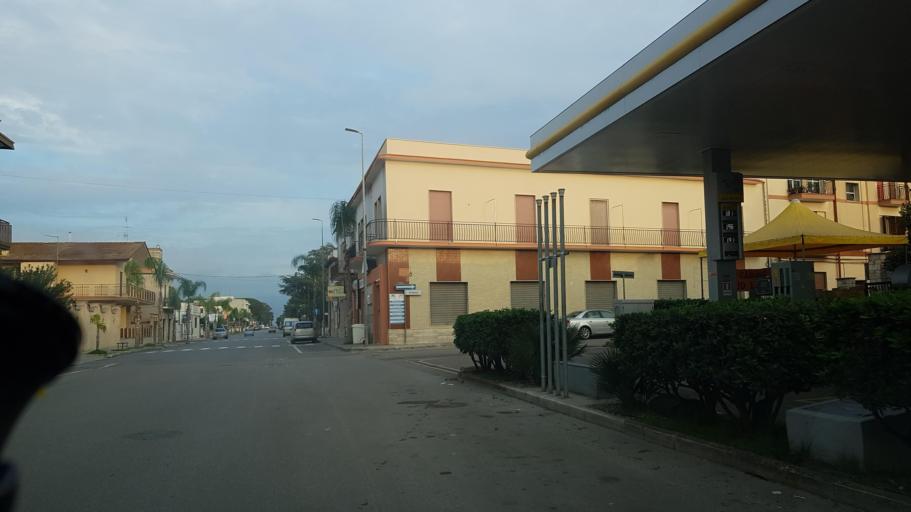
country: IT
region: Apulia
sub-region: Provincia di Brindisi
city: Latiano
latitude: 40.5531
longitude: 17.7254
